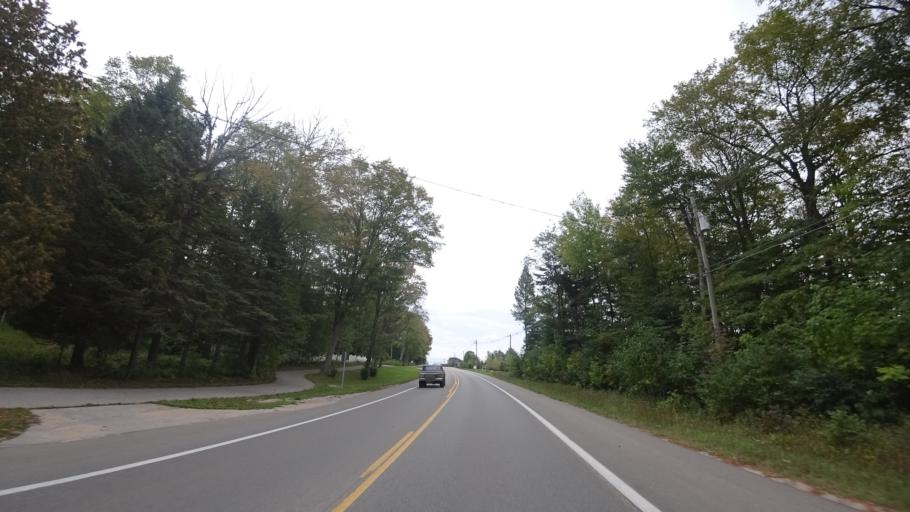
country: US
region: Michigan
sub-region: Emmet County
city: Petoskey
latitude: 45.4280
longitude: -84.9179
